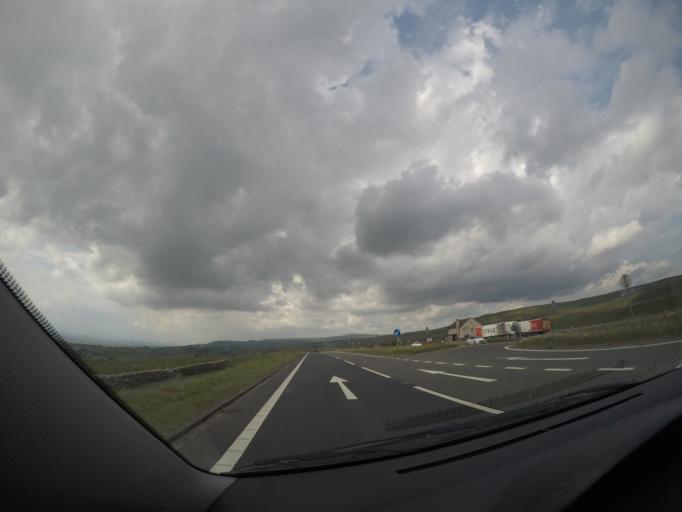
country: GB
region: England
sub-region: Cumbria
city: Kirkby Stephen
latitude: 54.5230
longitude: -2.2254
